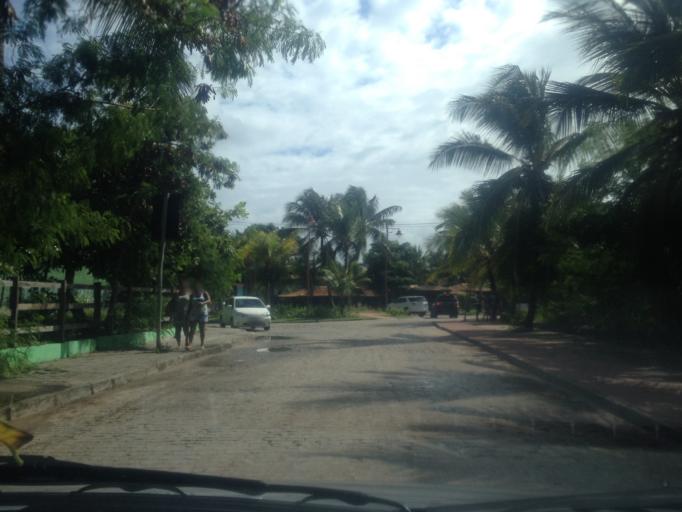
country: BR
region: Bahia
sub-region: Mata De Sao Joao
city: Mata de Sao Joao
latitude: -12.5751
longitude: -38.0047
